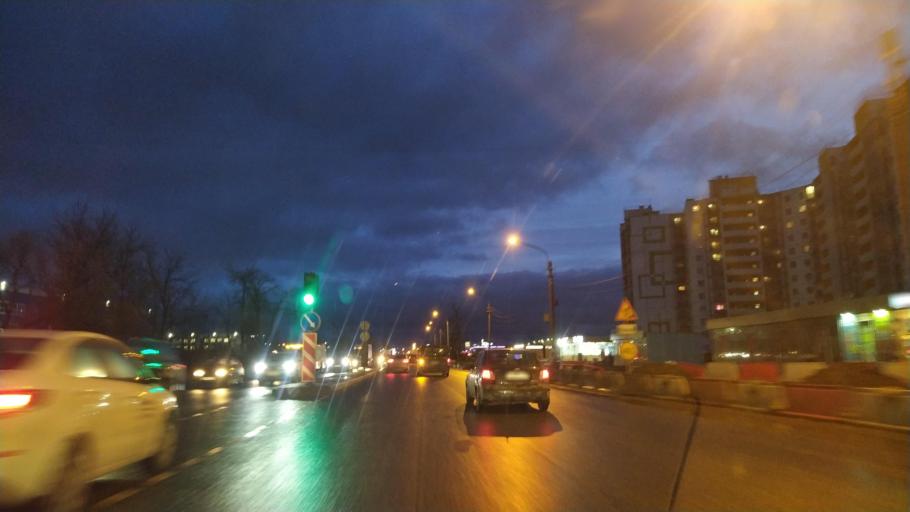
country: RU
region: St.-Petersburg
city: Petro-Slavyanka
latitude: 59.7609
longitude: 30.4741
